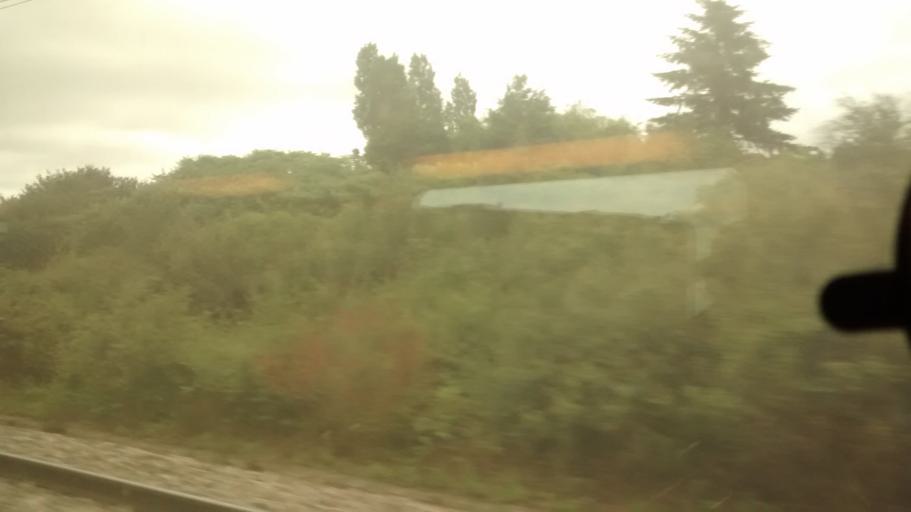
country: FR
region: Centre
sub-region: Departement d'Eure-et-Loir
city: Beville-le-Comte
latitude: 48.3523
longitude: 1.6906
